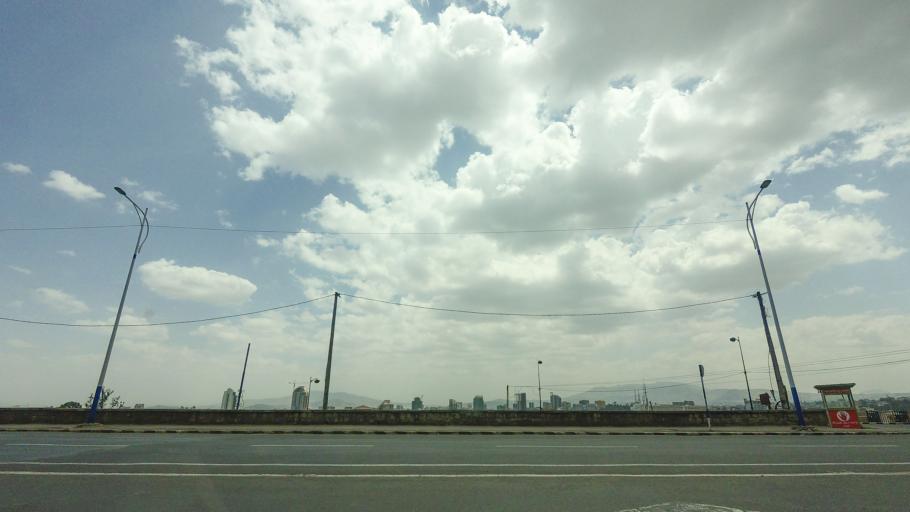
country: ET
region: Adis Abeba
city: Addis Ababa
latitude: 9.0226
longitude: 38.7611
